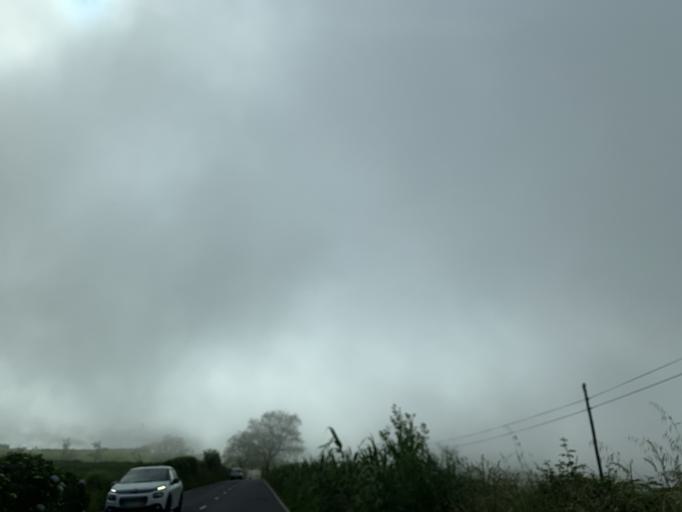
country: PT
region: Azores
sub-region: Ponta Delgada
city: Arrifes
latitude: 37.7745
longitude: -25.7460
